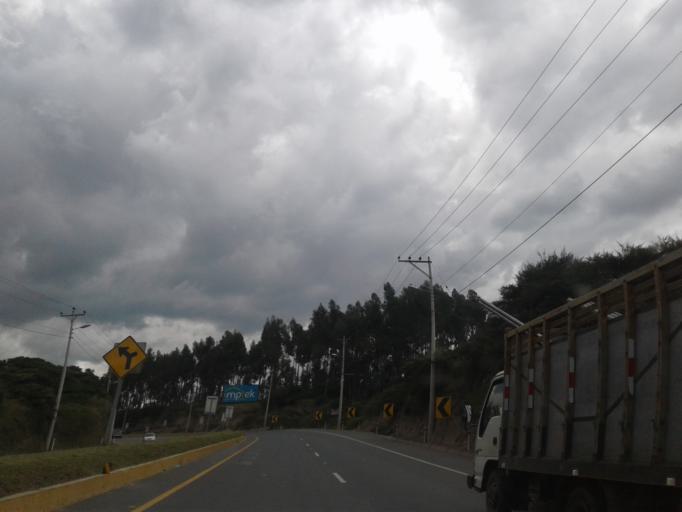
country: EC
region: Pichincha
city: Sangolqui
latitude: -0.3067
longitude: -78.3635
